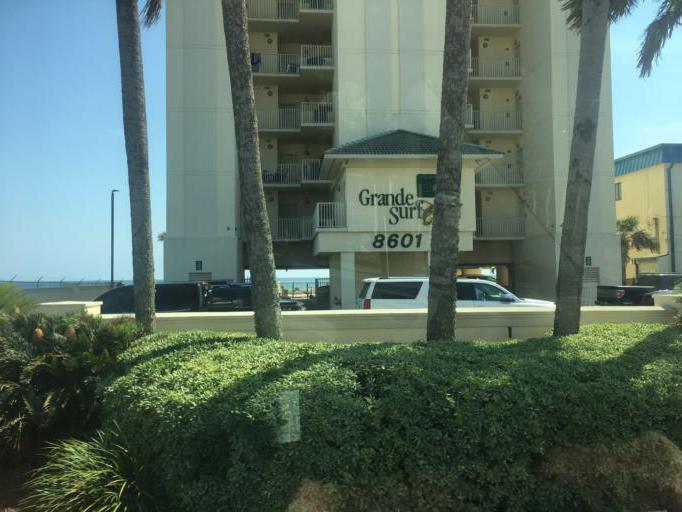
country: US
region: Florida
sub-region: Bay County
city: Panama City Beach
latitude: 30.1657
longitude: -85.7885
